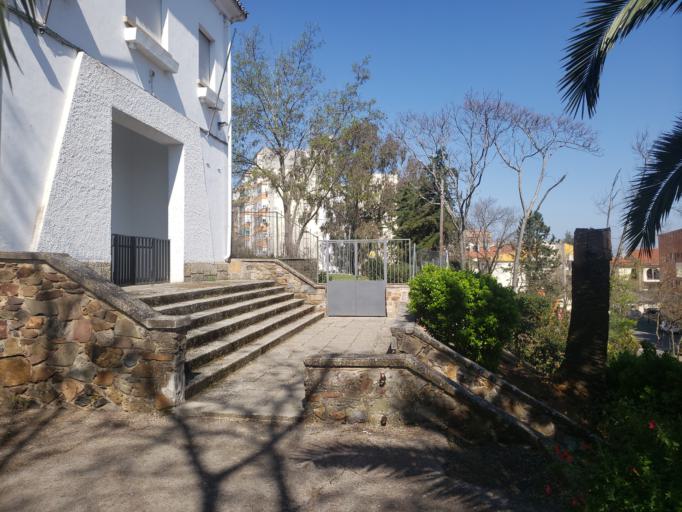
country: ES
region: Extremadura
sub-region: Provincia de Caceres
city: Caceres
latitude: 39.4681
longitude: -6.3688
